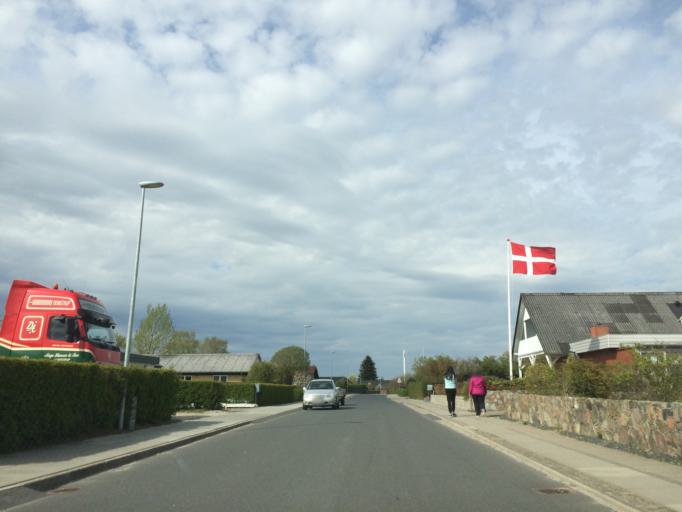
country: DK
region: Central Jutland
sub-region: Viborg Kommune
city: Bjerringbro
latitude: 56.2651
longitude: 9.7297
